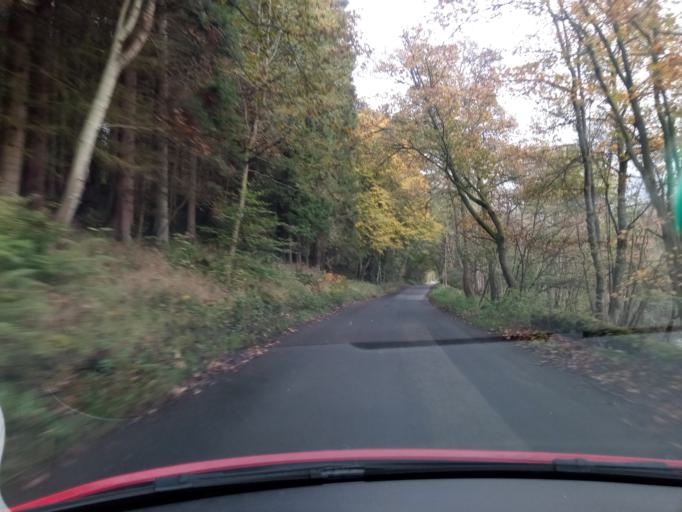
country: GB
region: Scotland
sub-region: The Scottish Borders
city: Innerleithen
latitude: 55.6261
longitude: -3.1025
